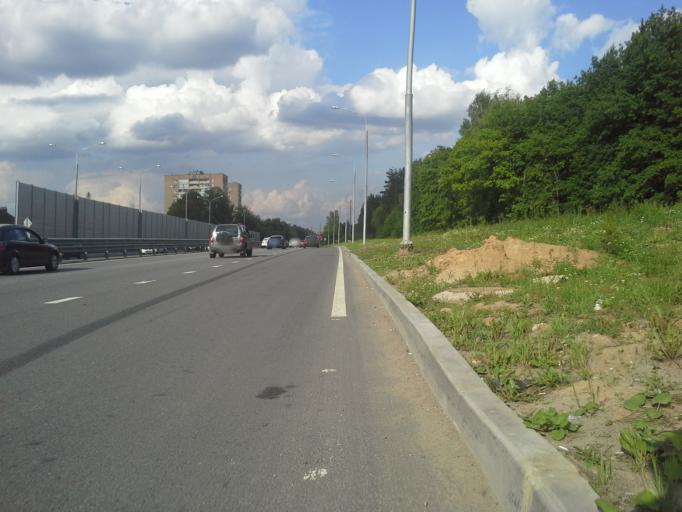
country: RU
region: Moskovskaya
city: Dubrovitsy
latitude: 55.4173
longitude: 37.5016
